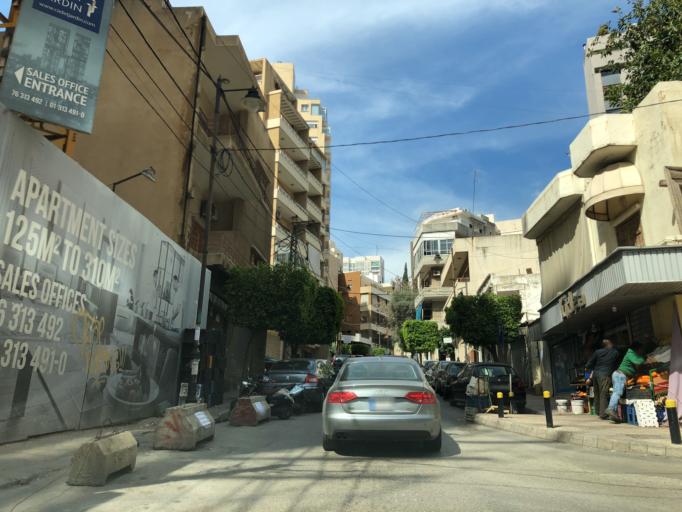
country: LB
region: Beyrouth
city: Beirut
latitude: 33.8837
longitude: 35.5190
